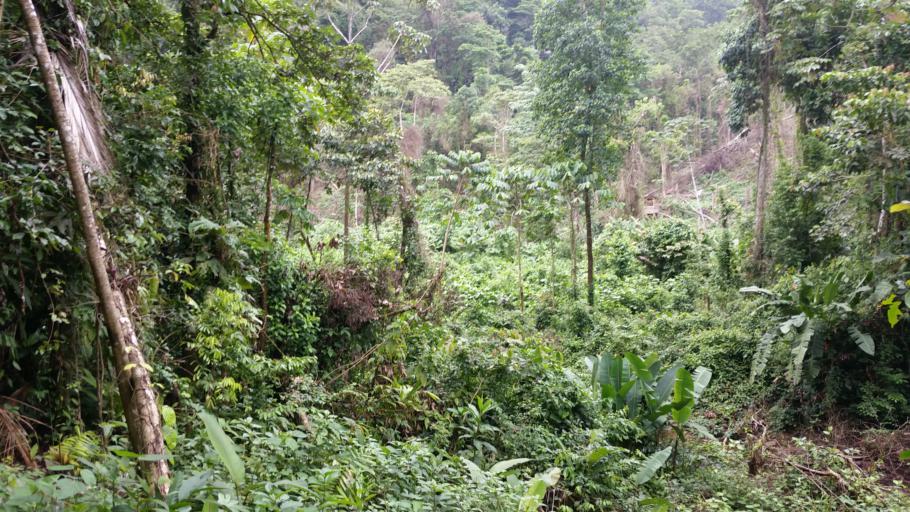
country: NI
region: Atlantico Norte (RAAN)
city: Bonanza
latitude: 14.0224
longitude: -84.7389
